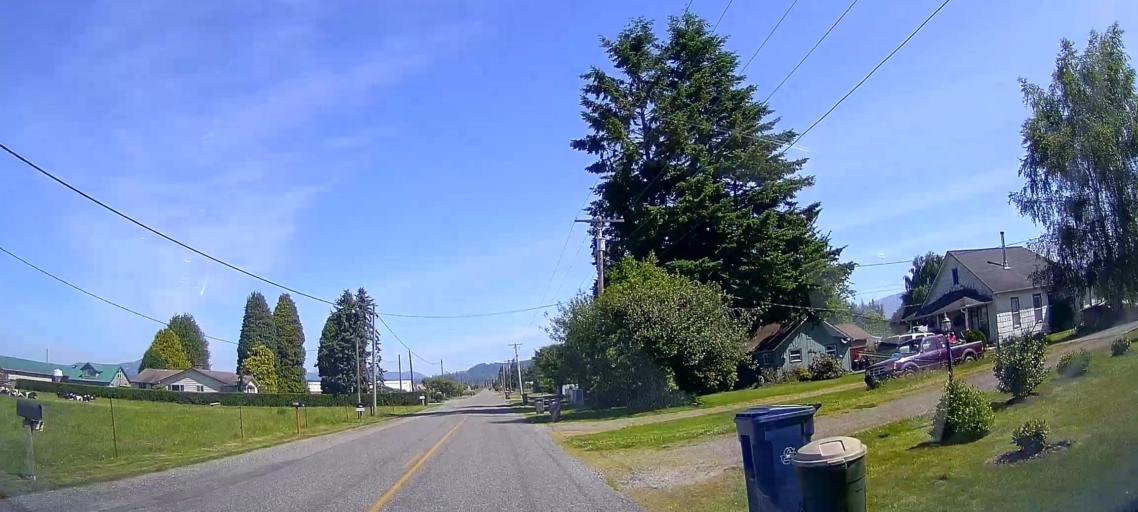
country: US
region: Washington
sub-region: Skagit County
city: Burlington
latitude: 48.4878
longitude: -122.3082
